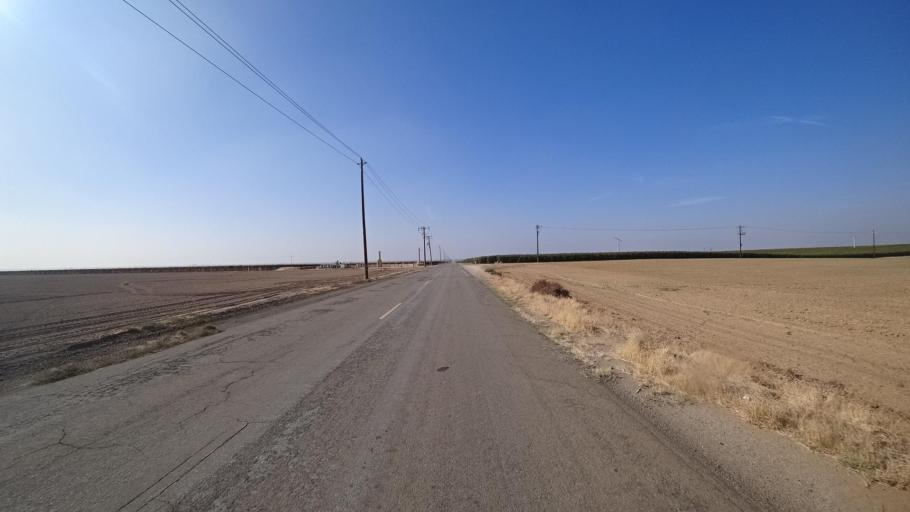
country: US
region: California
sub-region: Kern County
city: Oildale
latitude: 35.5299
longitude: -119.1146
